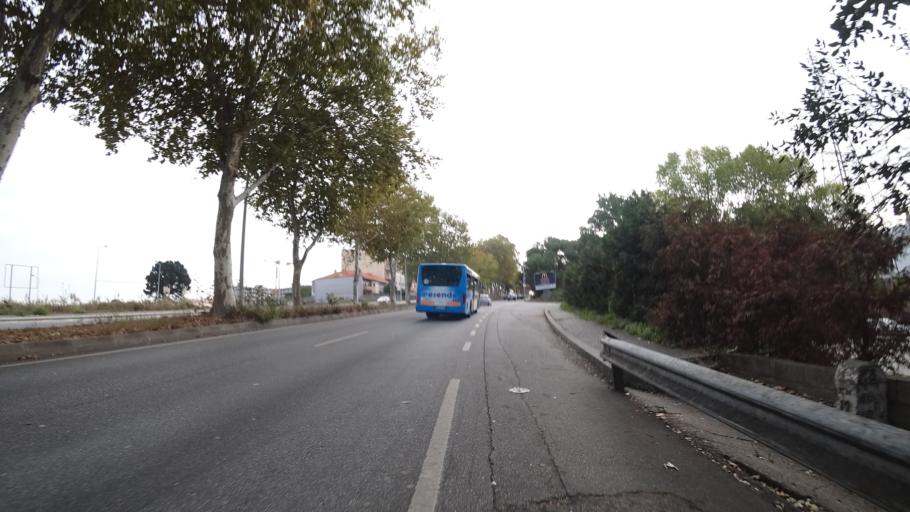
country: PT
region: Porto
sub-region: Matosinhos
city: Sao Mamede de Infesta
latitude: 41.1846
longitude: -8.6076
